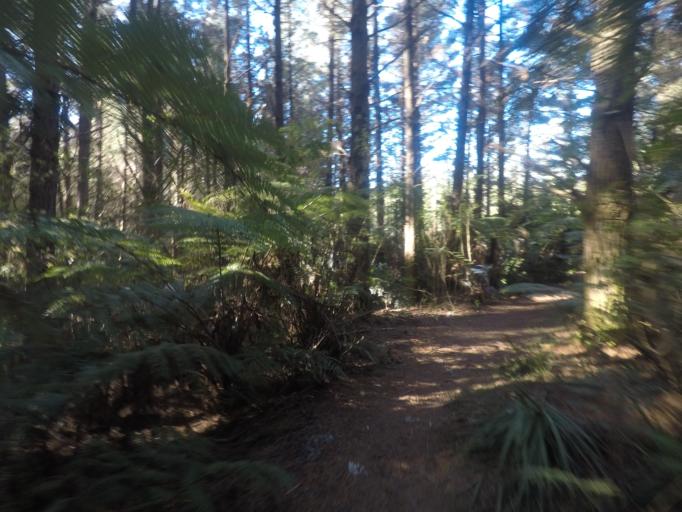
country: NZ
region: Auckland
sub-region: Auckland
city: Muriwai Beach
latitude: -36.7532
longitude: 174.5647
